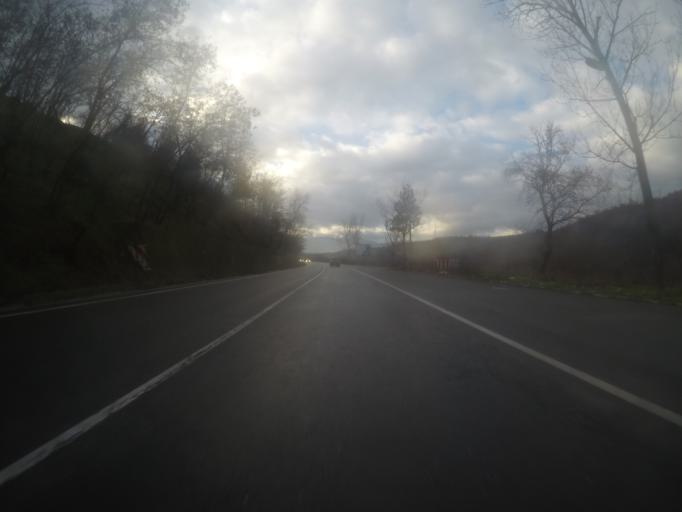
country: BG
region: Blagoevgrad
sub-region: Obshtina Simitli
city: Simitli
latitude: 41.9121
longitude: 23.1163
